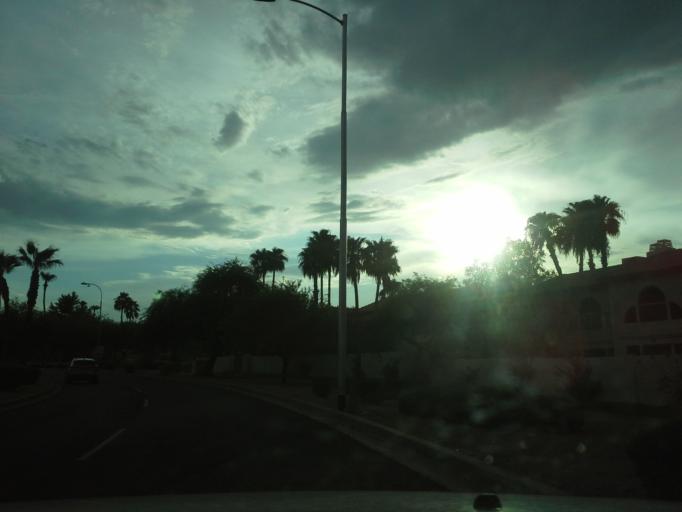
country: US
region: Arizona
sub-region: Maricopa County
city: Guadalupe
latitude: 33.3641
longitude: -111.9736
